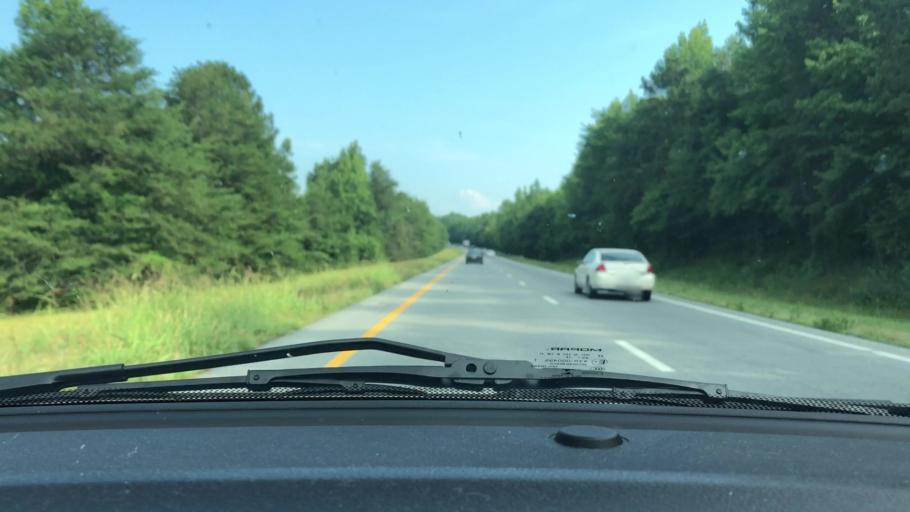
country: US
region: North Carolina
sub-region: Randolph County
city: Liberty
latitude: 35.8723
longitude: -79.6310
